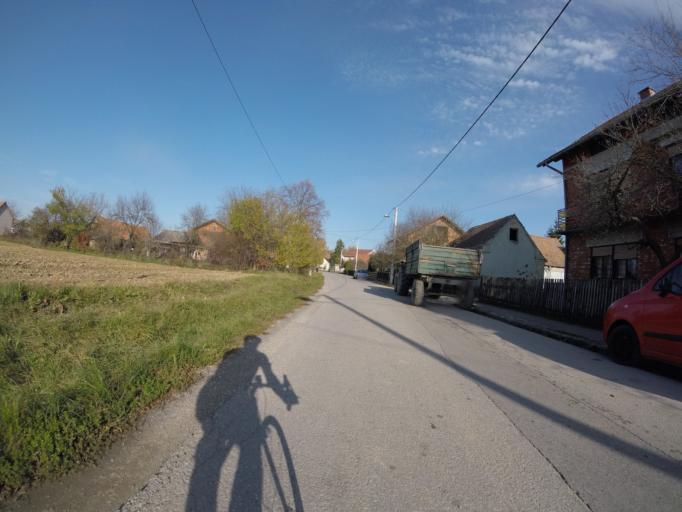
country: HR
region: Zagrebacka
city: Mraclin
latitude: 45.6630
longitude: 16.0846
